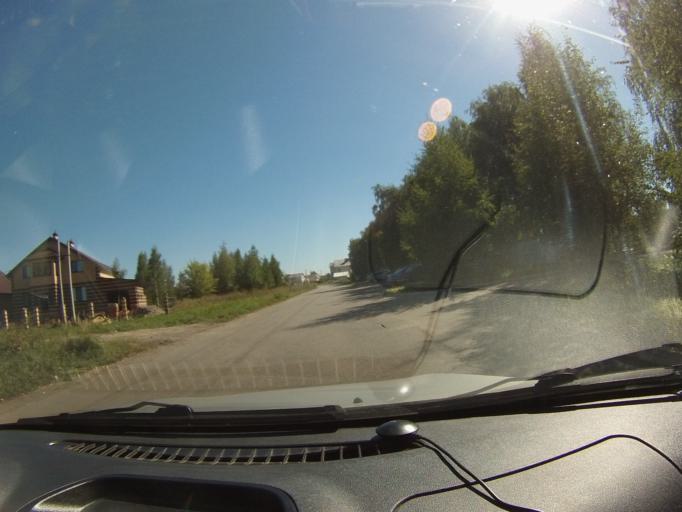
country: RU
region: Tambov
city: Komsomolets
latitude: 52.7672
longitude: 41.3619
